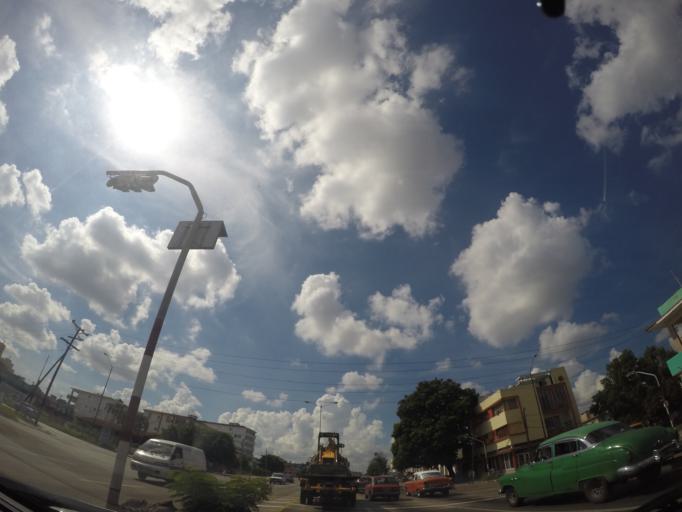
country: CU
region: La Habana
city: Cerro
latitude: 23.1122
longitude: -82.4180
